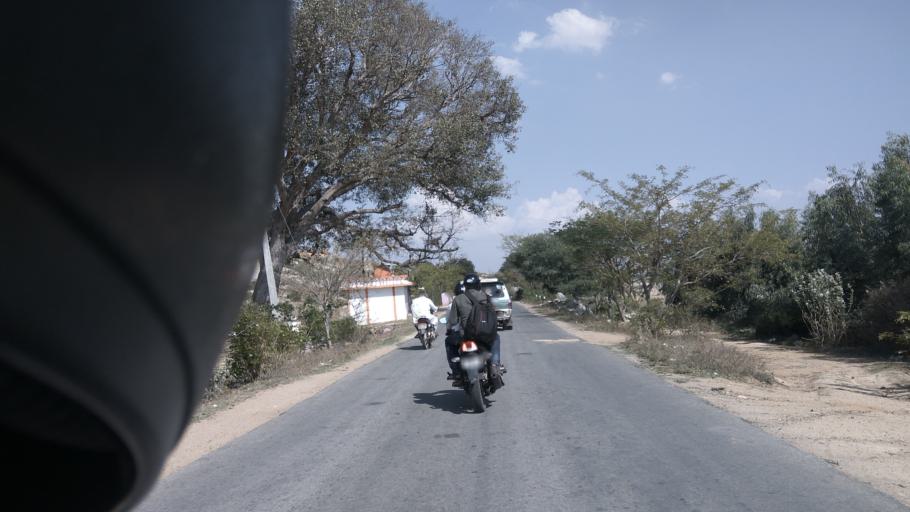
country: IN
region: Karnataka
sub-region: Kolar
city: Mulbagal
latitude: 13.1644
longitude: 78.3760
